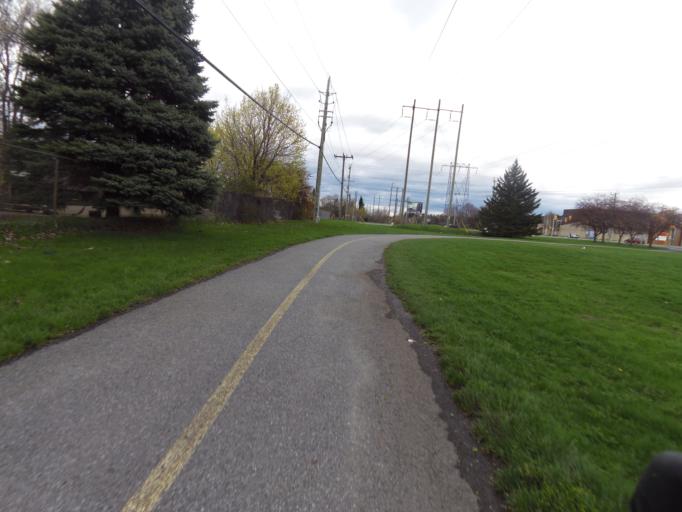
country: CA
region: Ontario
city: Bells Corners
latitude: 45.3272
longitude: -75.7812
